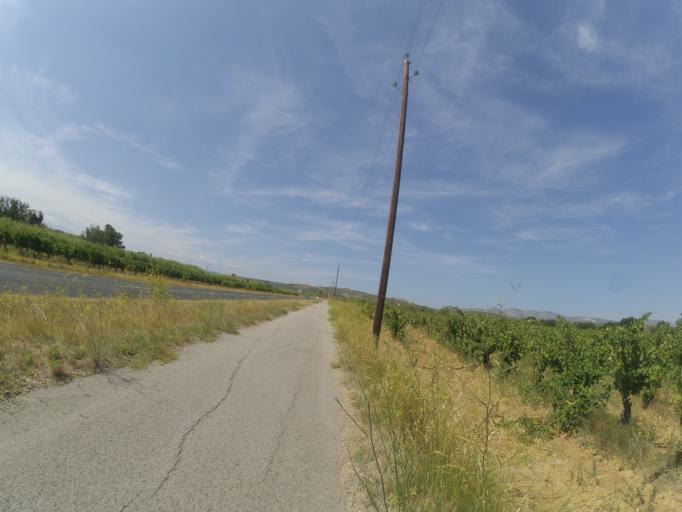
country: FR
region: Languedoc-Roussillon
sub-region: Departement des Pyrenees-Orientales
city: Peyrestortes
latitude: 42.7565
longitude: 2.8363
